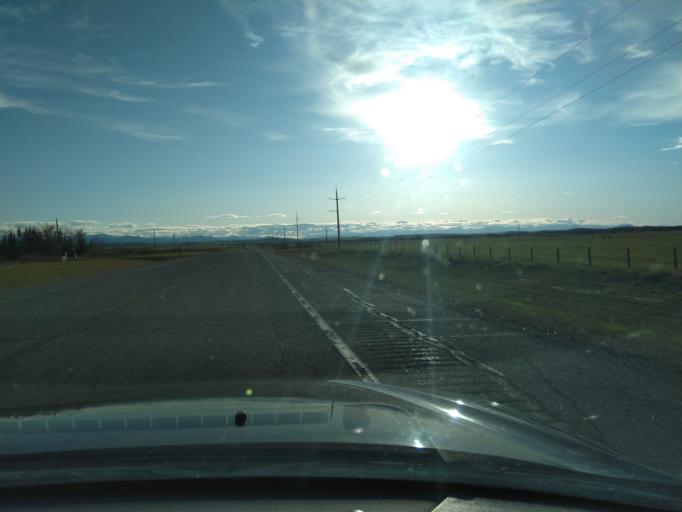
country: CA
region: Alberta
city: Cochrane
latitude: 51.0234
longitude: -114.3880
